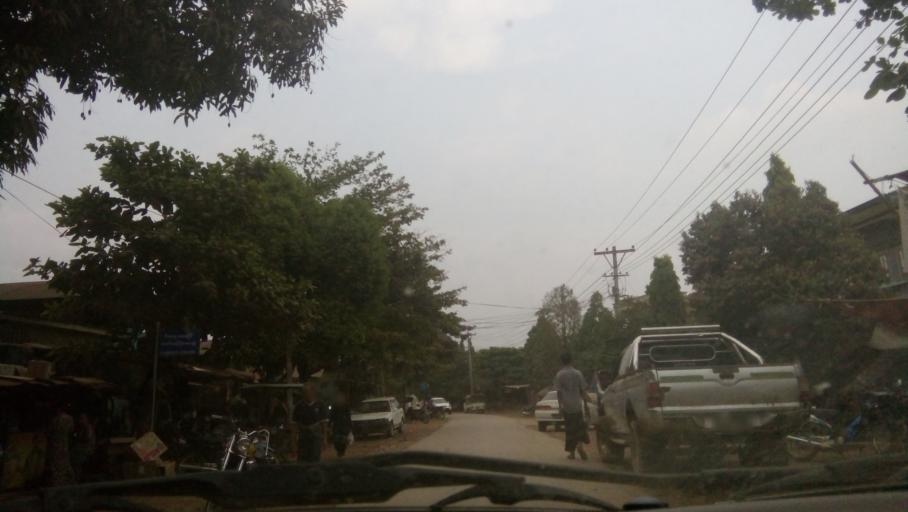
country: MM
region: Kayin
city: Hpa-an
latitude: 17.1205
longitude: 97.8191
